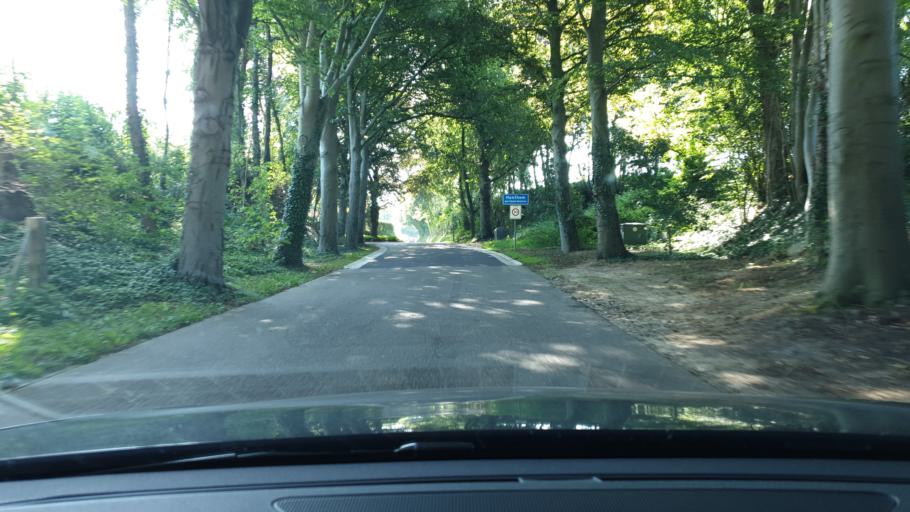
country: NL
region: Limburg
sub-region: Eijsden-Margraten
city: Margraten
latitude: 50.8180
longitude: 5.7933
